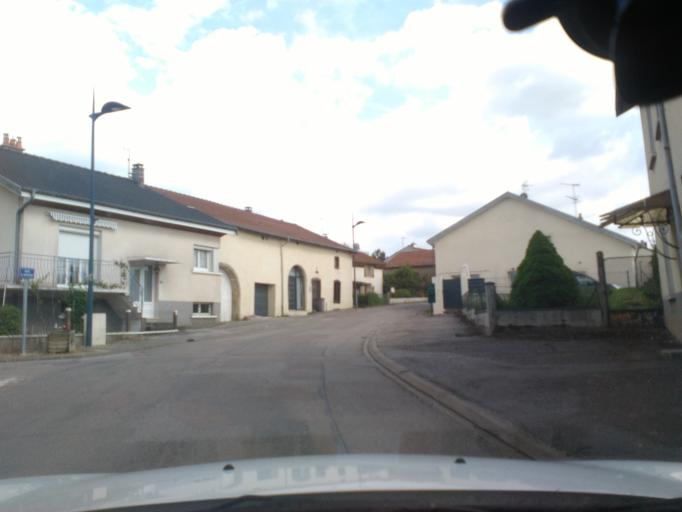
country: FR
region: Lorraine
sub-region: Departement des Vosges
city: Mirecourt
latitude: 48.3224
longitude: 6.1471
